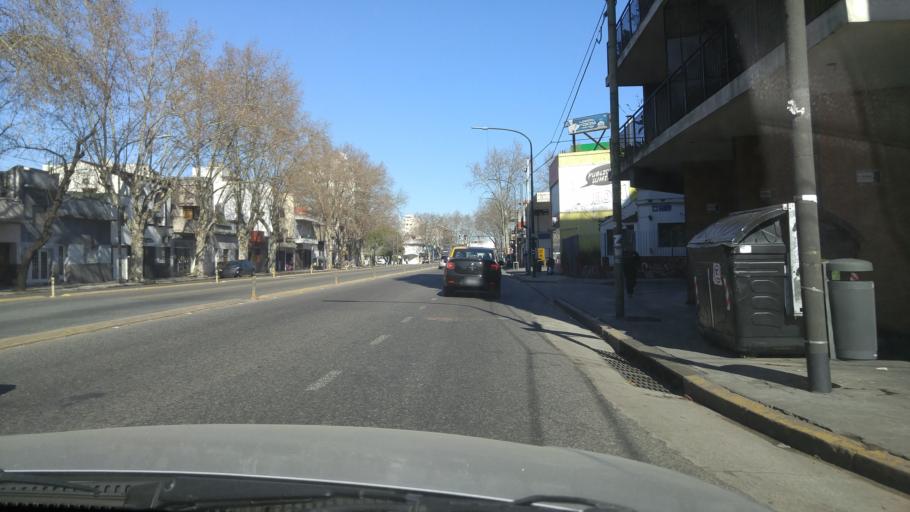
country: AR
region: Buenos Aires F.D.
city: Villa Santa Rita
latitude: -34.6086
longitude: -58.4645
